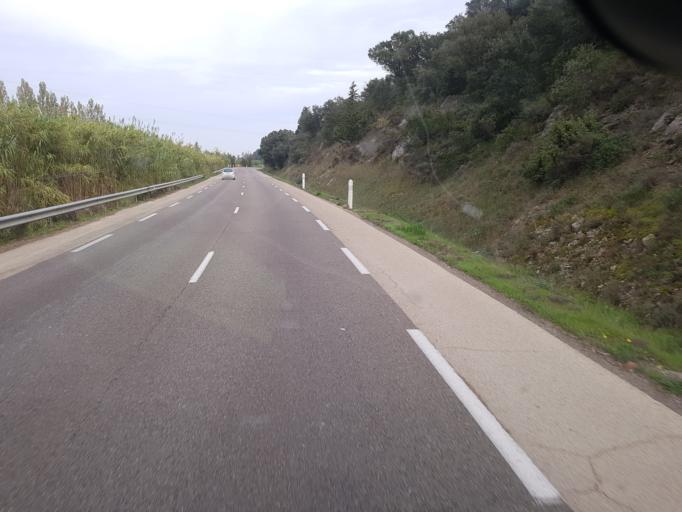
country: FR
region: Languedoc-Roussillon
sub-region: Departement du Gard
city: Aramon
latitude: 43.8958
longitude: 4.7108
